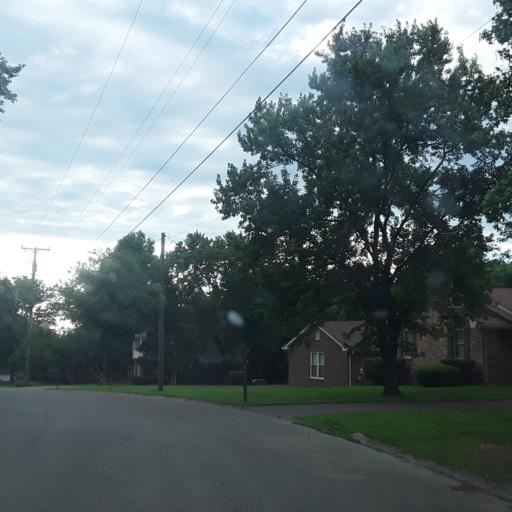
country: US
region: Tennessee
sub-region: Wilson County
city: Green Hill
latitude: 36.1687
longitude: -86.5876
